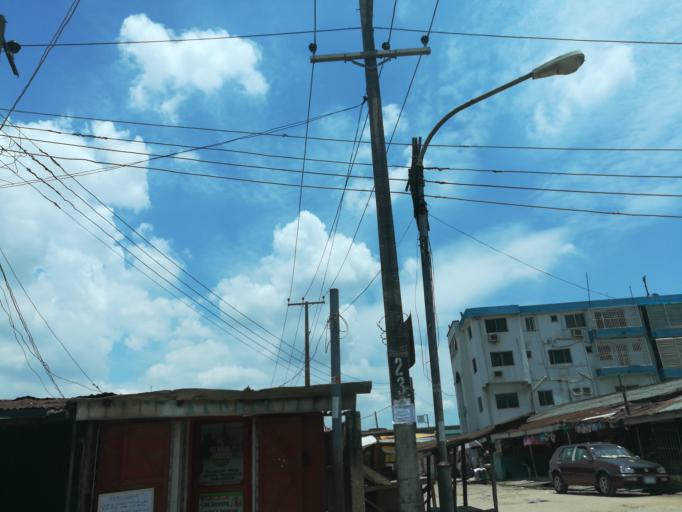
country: NG
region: Lagos
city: Ebute Ikorodu
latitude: 6.6030
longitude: 3.4924
